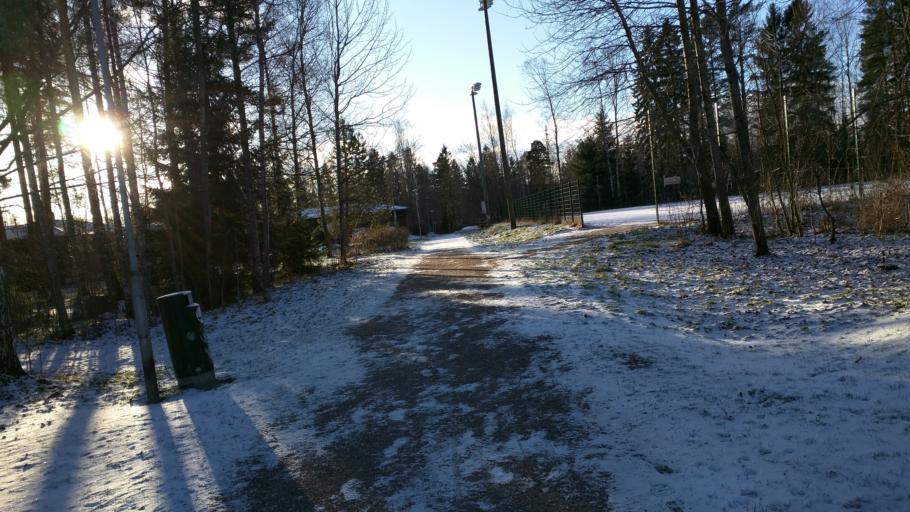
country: FI
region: Uusimaa
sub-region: Helsinki
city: Kilo
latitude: 60.2439
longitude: 24.7654
